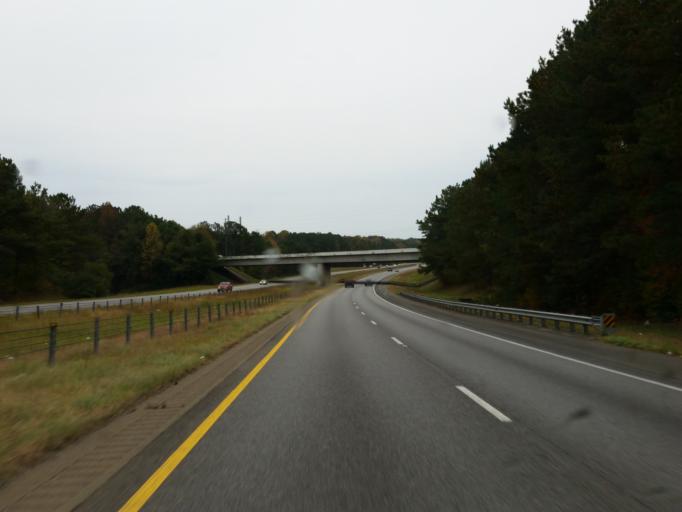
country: US
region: Georgia
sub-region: Cherokee County
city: Holly Springs
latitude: 34.1871
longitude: -84.5061
